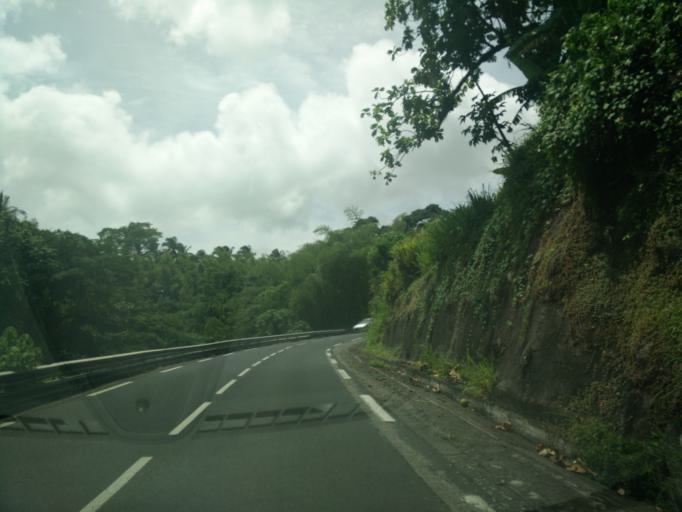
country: MQ
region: Martinique
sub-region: Martinique
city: Saint-Pierre
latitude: 14.7576
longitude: -61.1633
